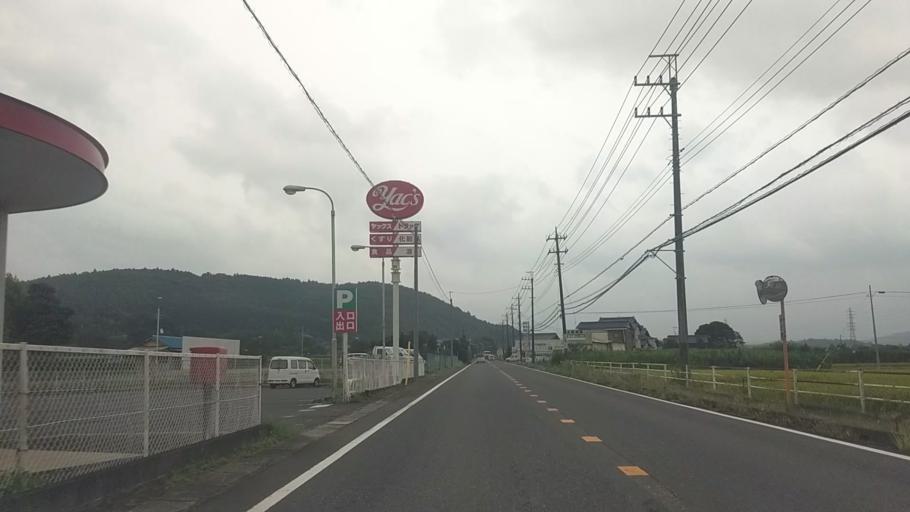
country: JP
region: Chiba
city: Kisarazu
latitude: 35.3089
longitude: 140.0664
